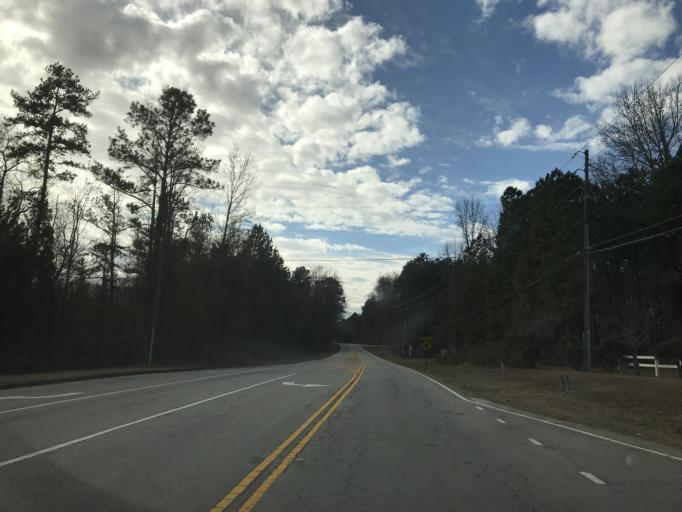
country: US
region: Georgia
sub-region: Douglas County
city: Douglasville
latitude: 33.7904
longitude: -84.7789
